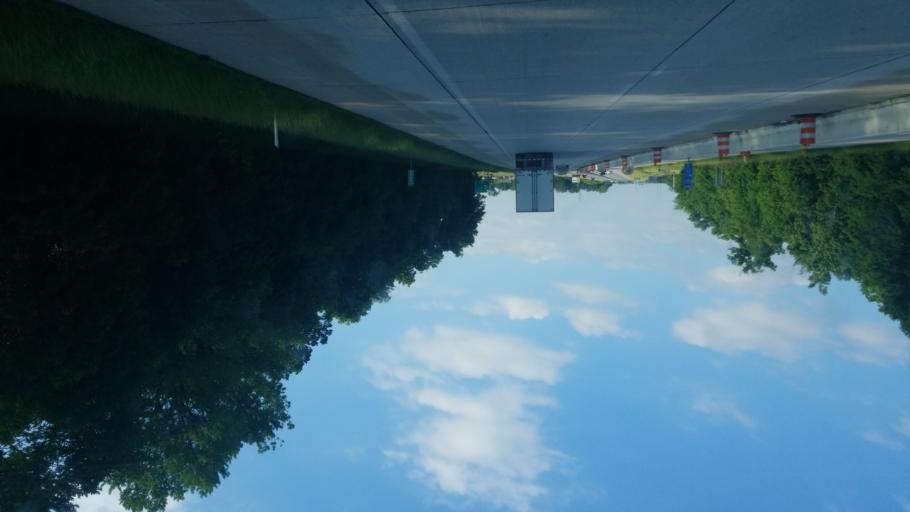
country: US
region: Indiana
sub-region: Allen County
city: New Haven
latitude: 41.1003
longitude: -84.9961
